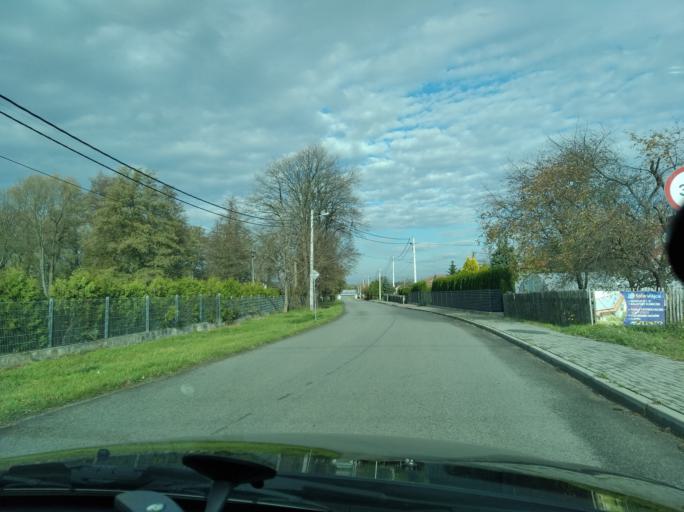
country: PL
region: Subcarpathian Voivodeship
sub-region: Powiat debicki
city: Brzeznica
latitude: 50.0685
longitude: 21.5277
